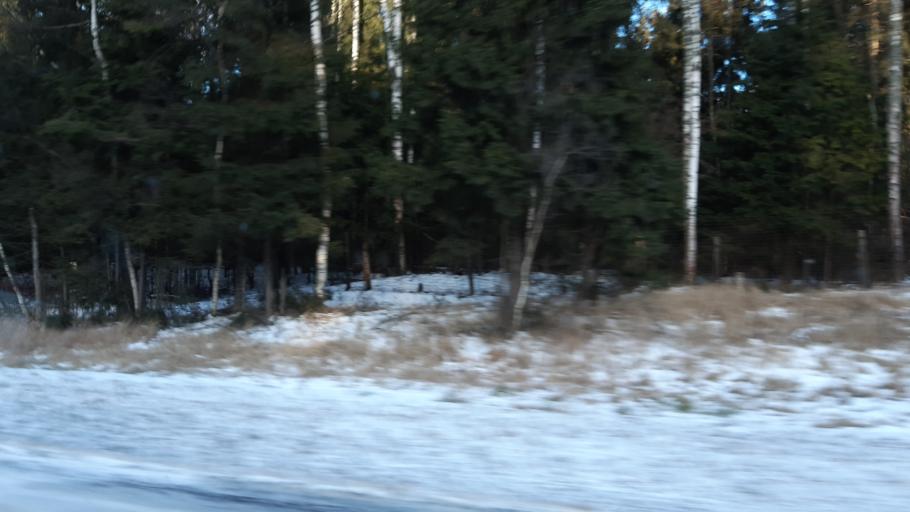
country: RU
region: Vladimir
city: Arsaki
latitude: 56.2652
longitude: 38.4293
